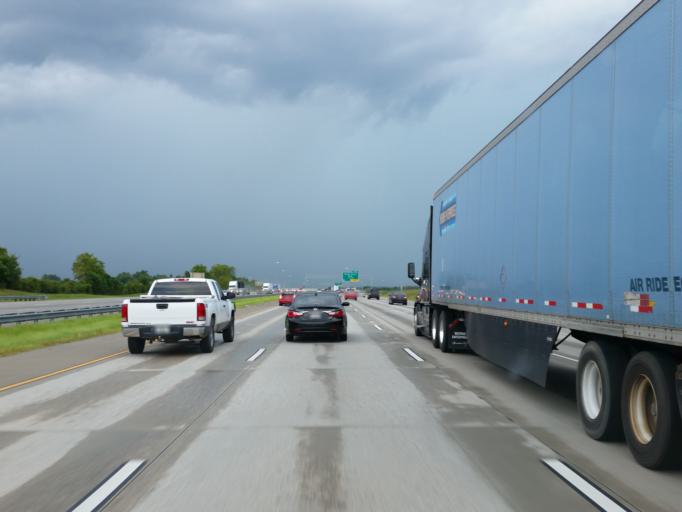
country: US
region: Georgia
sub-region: Peach County
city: Byron
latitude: 32.7262
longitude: -83.7265
